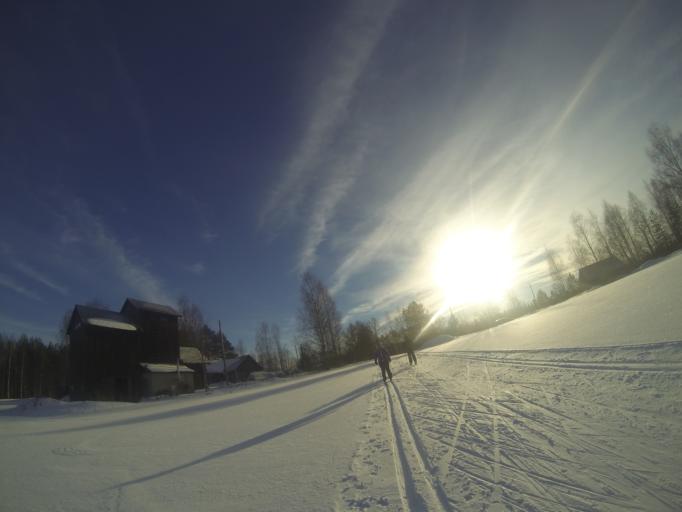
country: FI
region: Southern Savonia
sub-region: Savonlinna
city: Savonlinna
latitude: 61.9388
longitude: 28.9183
